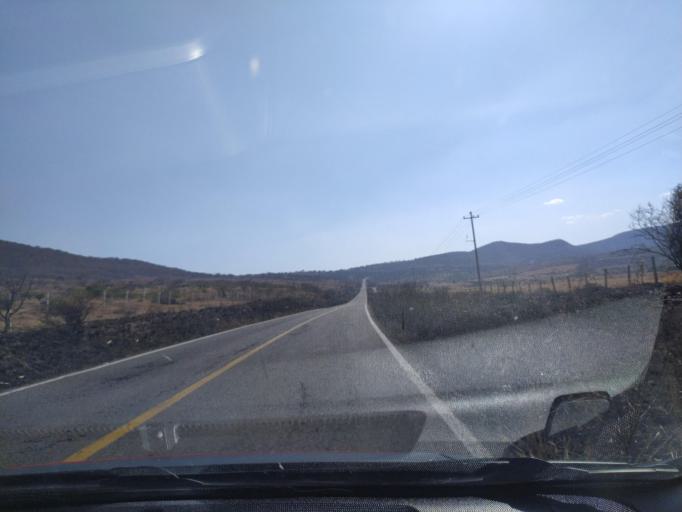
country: MX
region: Guanajuato
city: Ciudad Manuel Doblado
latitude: 20.6350
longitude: -101.9751
